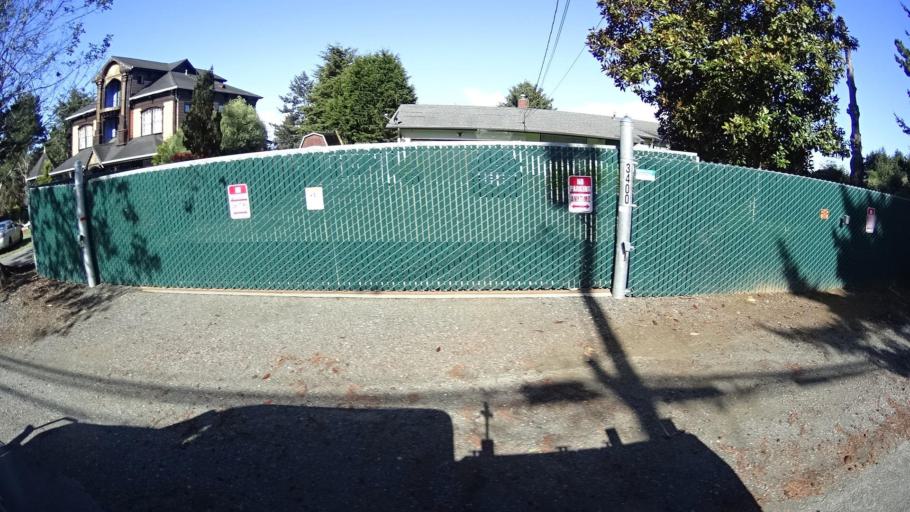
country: US
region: California
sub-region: Humboldt County
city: McKinleyville
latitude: 40.9651
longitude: -124.0960
